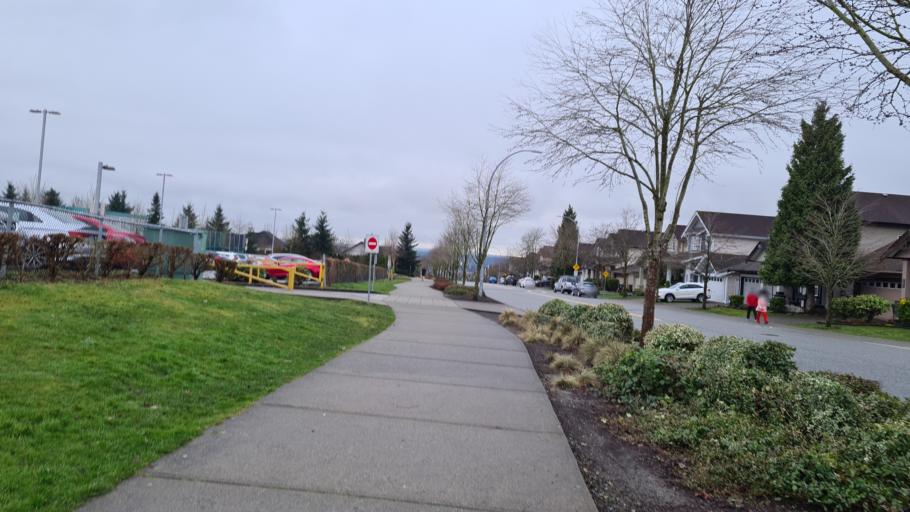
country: CA
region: British Columbia
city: Langley
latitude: 49.1320
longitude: -122.6645
